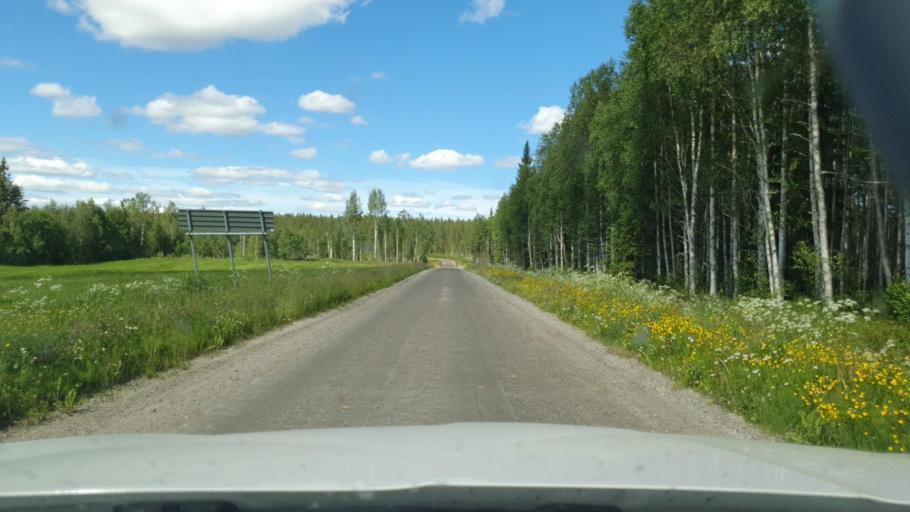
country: SE
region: Norrbotten
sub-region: Pitea Kommun
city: Roknas
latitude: 65.1577
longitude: 21.1582
